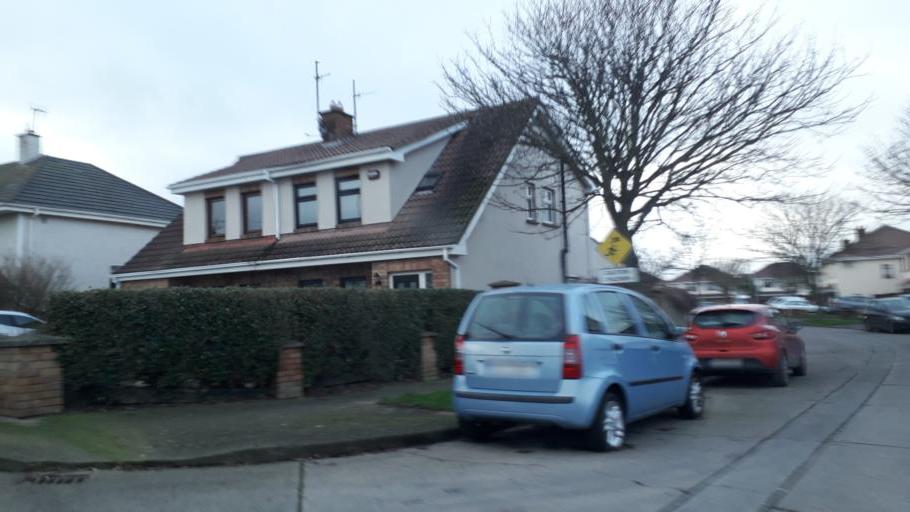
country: IE
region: Leinster
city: An Ros
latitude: 53.5216
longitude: -6.0795
